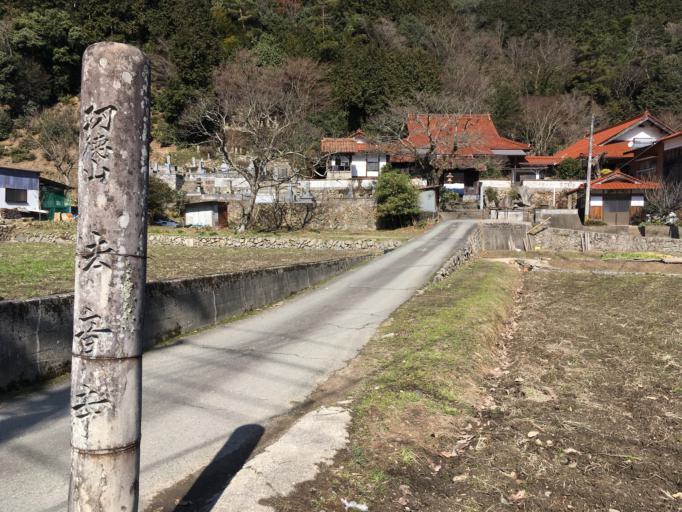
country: JP
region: Shimane
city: Masuda
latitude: 34.4521
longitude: 131.7609
